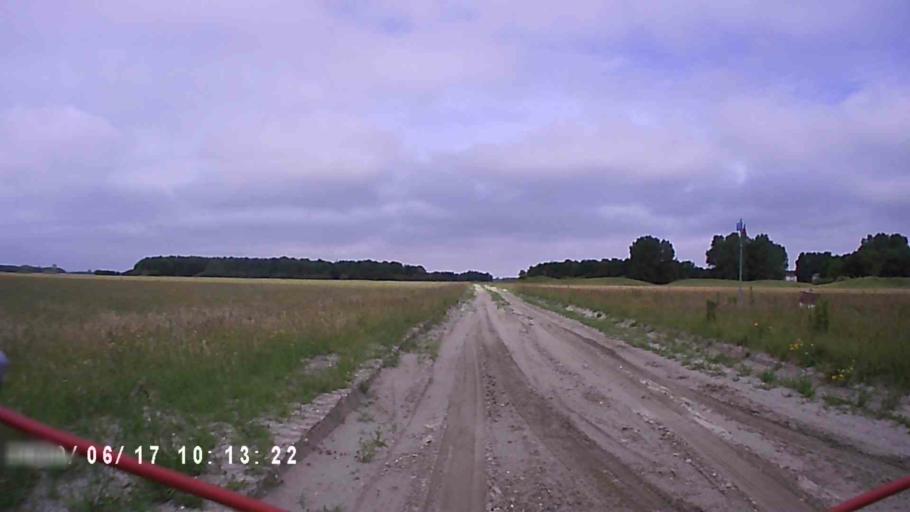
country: NL
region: Groningen
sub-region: Gemeente De Marne
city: Ulrum
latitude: 53.3831
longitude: 6.2641
